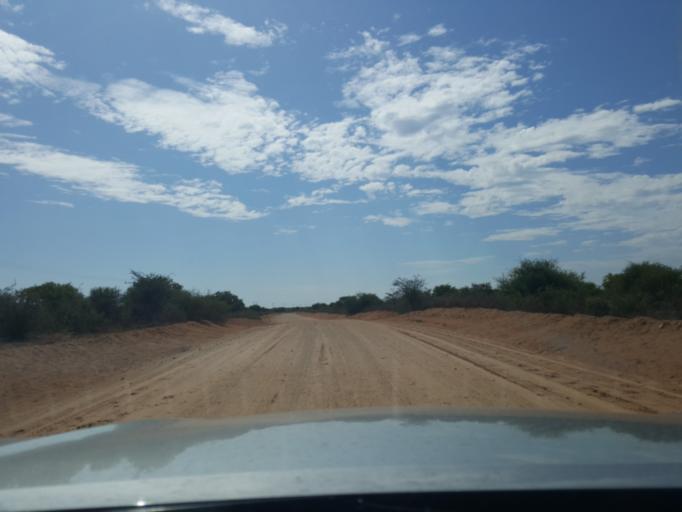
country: BW
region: Kweneng
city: Khudumelapye
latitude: -23.8621
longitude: 24.8863
